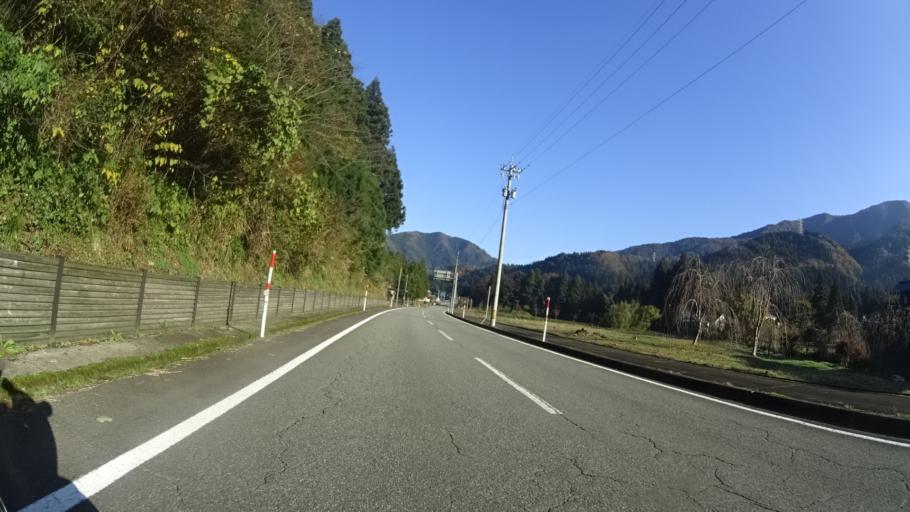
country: JP
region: Fukui
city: Maruoka
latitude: 36.1570
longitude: 136.3321
